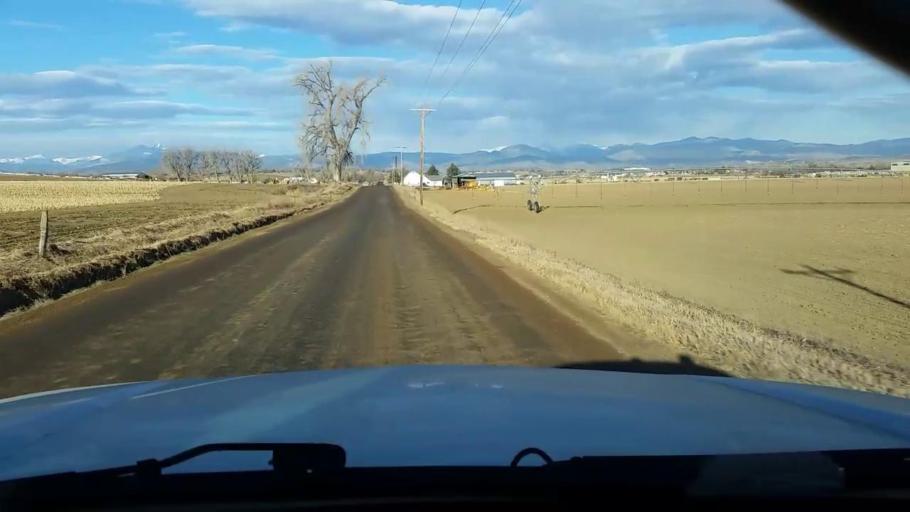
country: US
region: Colorado
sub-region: Larimer County
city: Campion
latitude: 40.3710
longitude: -105.0437
